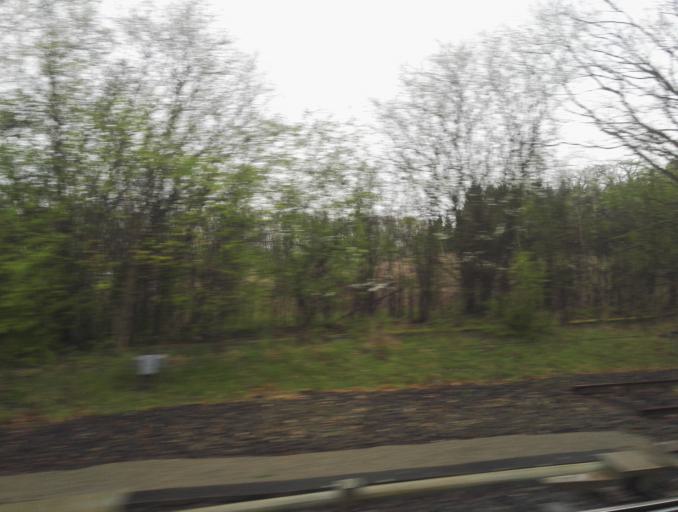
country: DE
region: Lower Saxony
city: Alt Wallmoden
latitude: 52.0388
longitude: 10.3275
